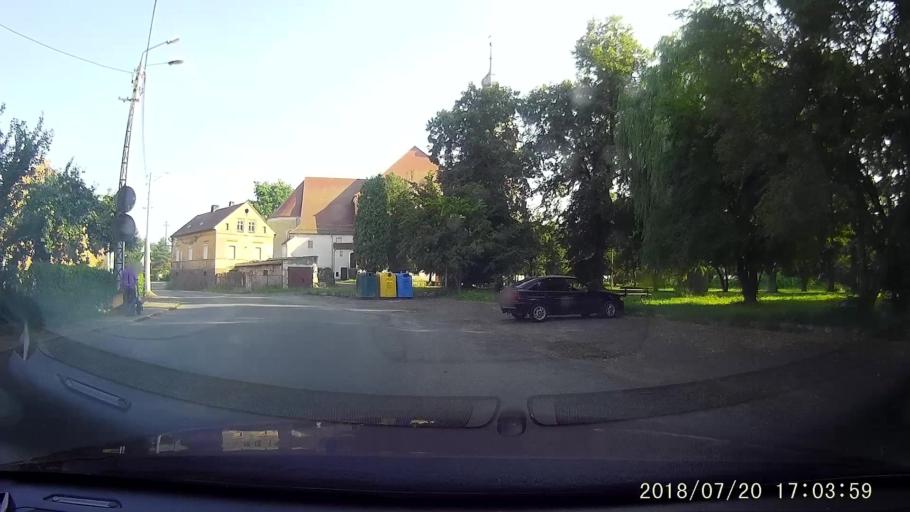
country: PL
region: Lower Silesian Voivodeship
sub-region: Powiat lubanski
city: Lesna
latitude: 51.0264
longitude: 15.2607
